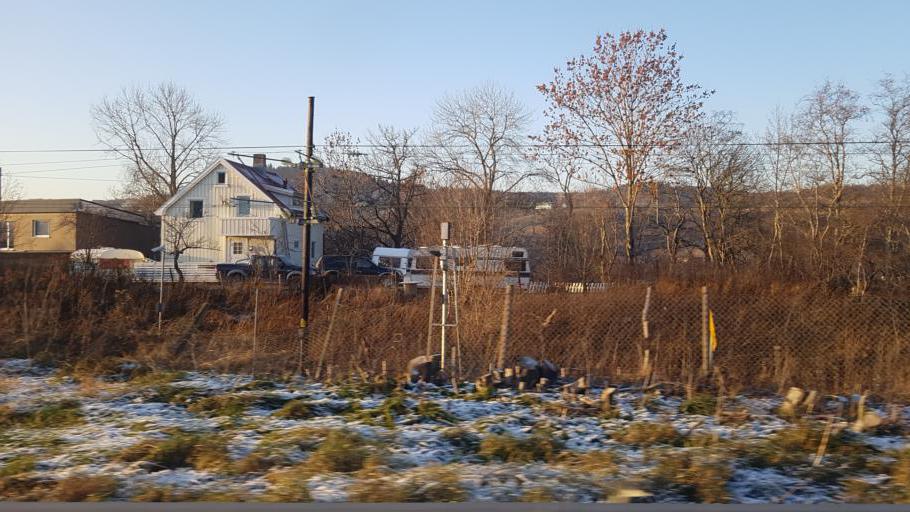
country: NO
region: Sor-Trondelag
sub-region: Melhus
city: Melhus
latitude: 63.2917
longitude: 10.2759
